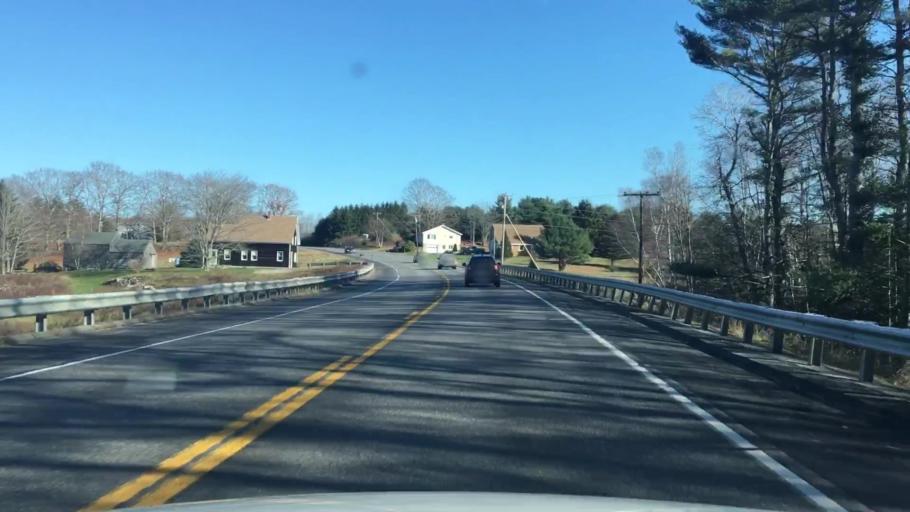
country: US
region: Maine
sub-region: Knox County
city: Union
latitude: 44.2119
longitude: -69.2120
